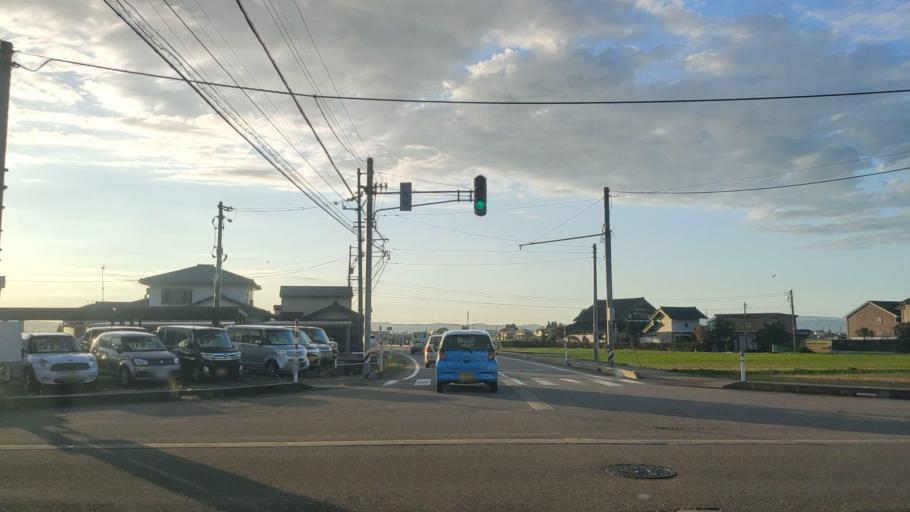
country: JP
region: Toyama
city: Nanto-shi
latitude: 36.5986
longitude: 136.9439
